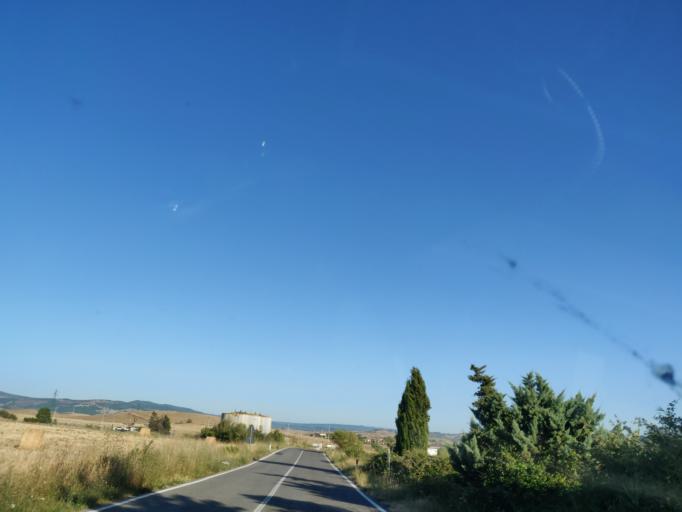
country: IT
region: Tuscany
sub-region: Provincia di Siena
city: Piancastagnaio
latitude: 42.8273
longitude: 11.7223
